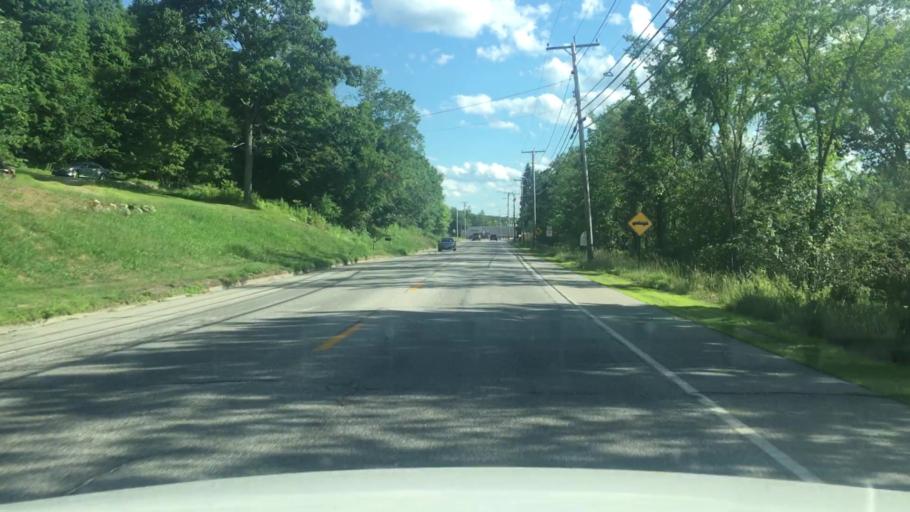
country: US
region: Maine
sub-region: Franklin County
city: Wilton
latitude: 44.5500
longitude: -70.2374
